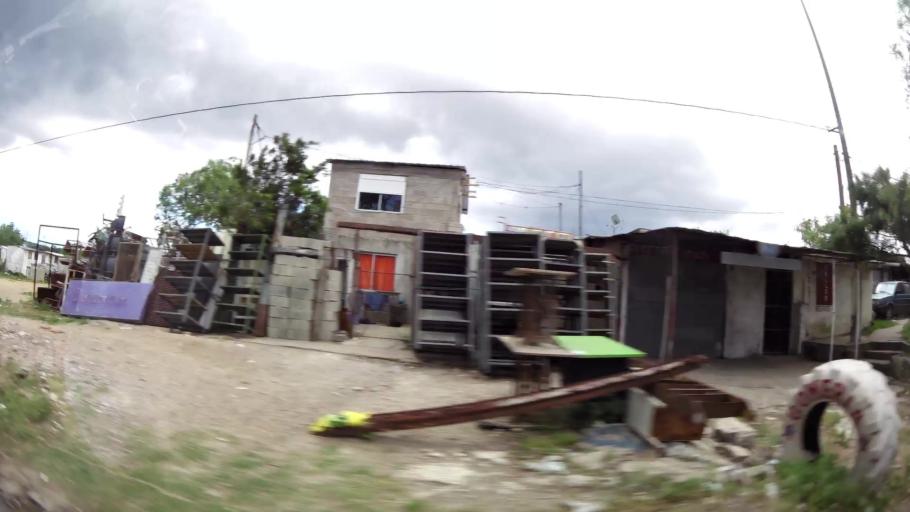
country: UY
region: Montevideo
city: Montevideo
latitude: -34.8339
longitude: -56.1682
